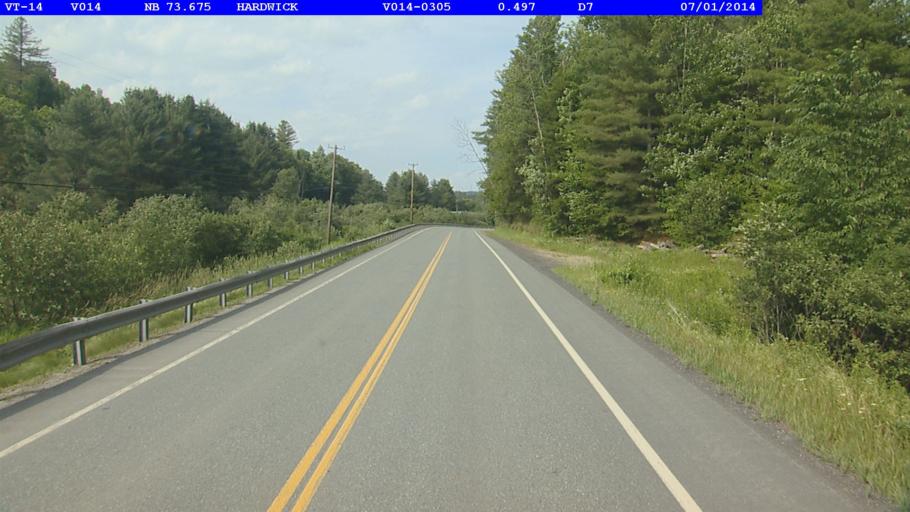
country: US
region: Vermont
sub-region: Caledonia County
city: Hardwick
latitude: 44.4922
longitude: -72.3771
